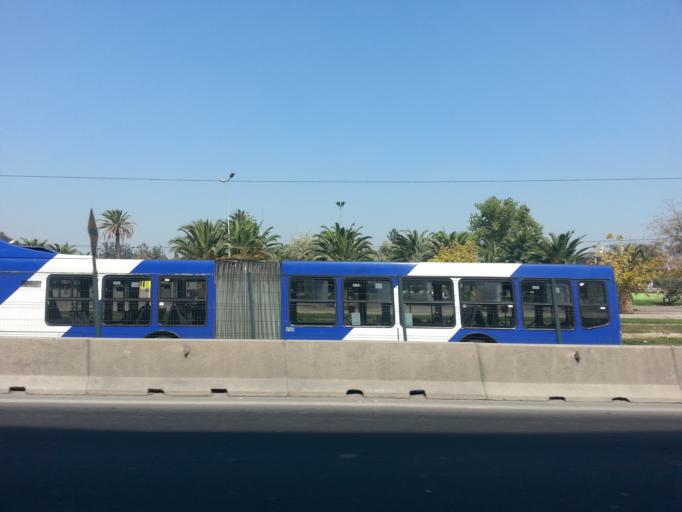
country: CL
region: Santiago Metropolitan
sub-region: Provincia de Santiago
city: La Pintana
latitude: -33.5413
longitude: -70.6439
